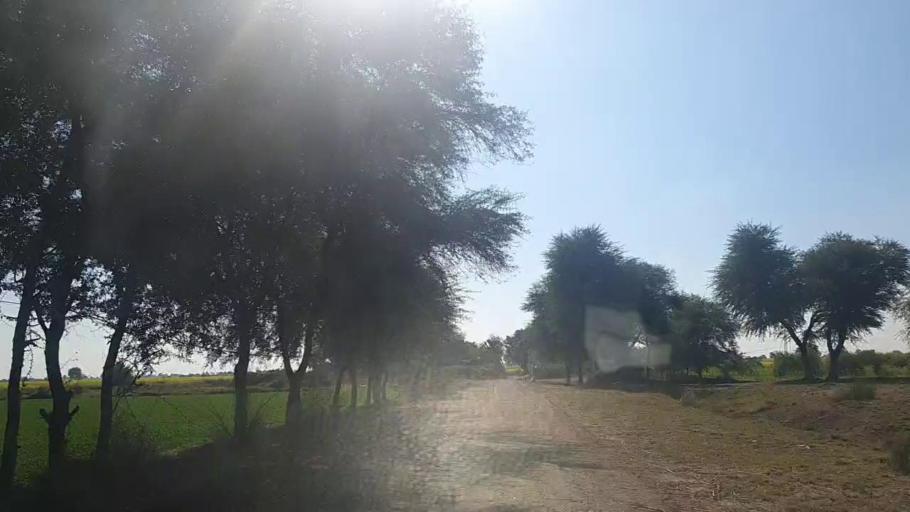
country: PK
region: Sindh
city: Sinjhoro
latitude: 26.1293
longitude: 68.8514
